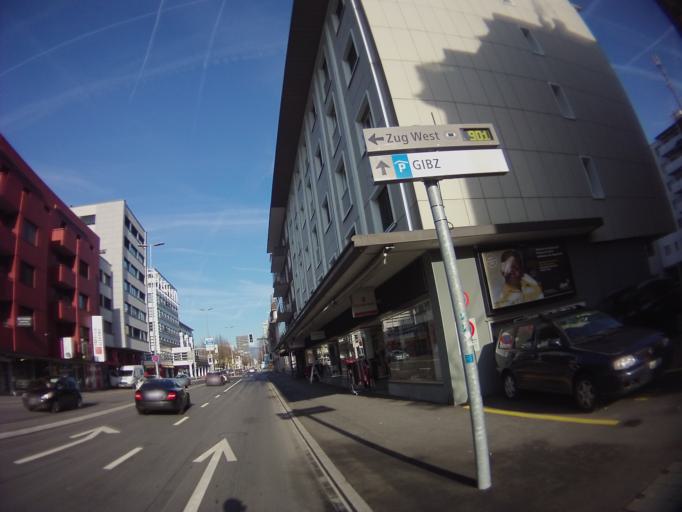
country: CH
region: Zug
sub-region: Zug
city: Zug
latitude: 47.1737
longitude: 8.5170
